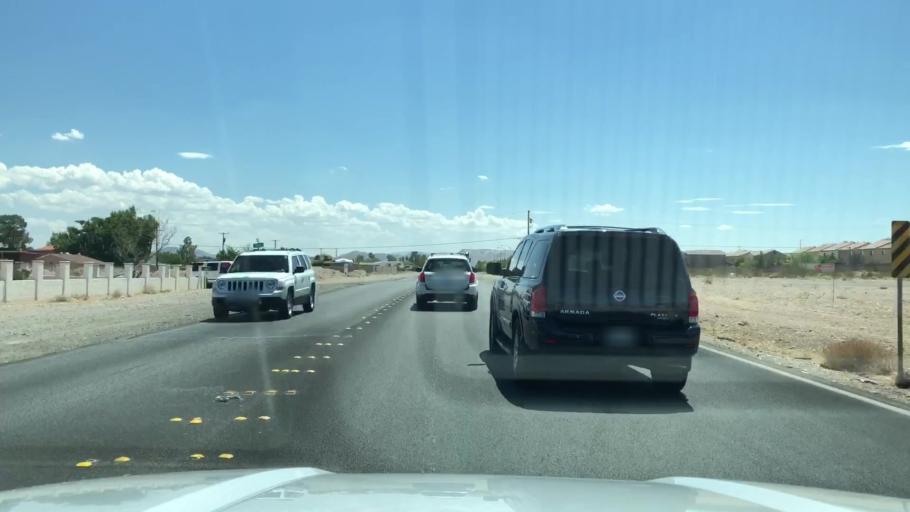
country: US
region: Nevada
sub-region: Clark County
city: Enterprise
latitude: 36.0558
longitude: -115.2079
